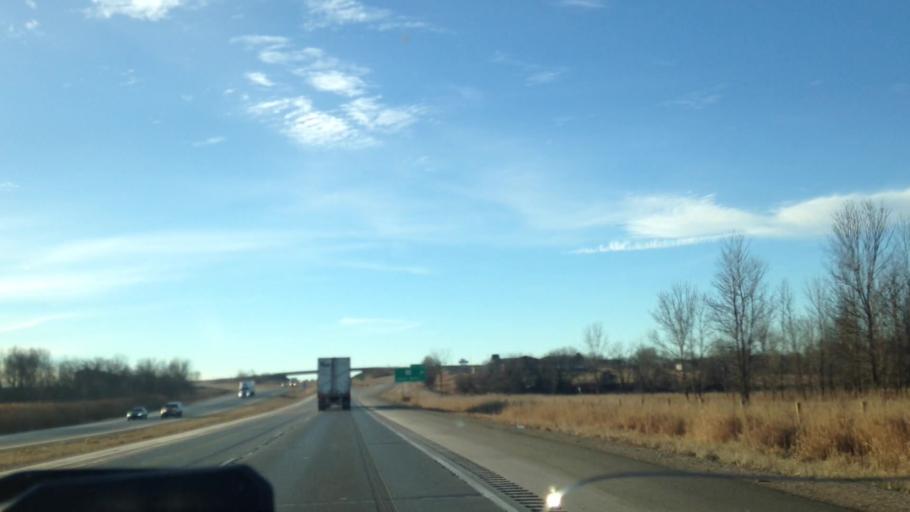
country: US
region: Wisconsin
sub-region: Dodge County
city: Theresa
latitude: 43.4800
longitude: -88.3670
